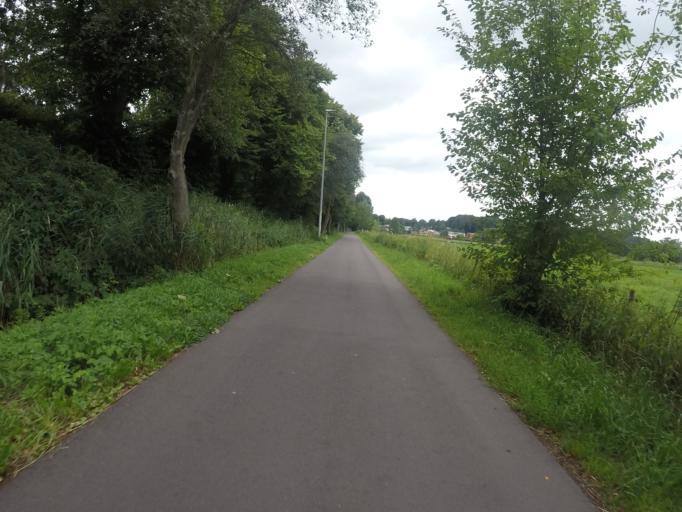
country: DE
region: Lower Saxony
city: Stade
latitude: 53.5979
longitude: 9.4633
